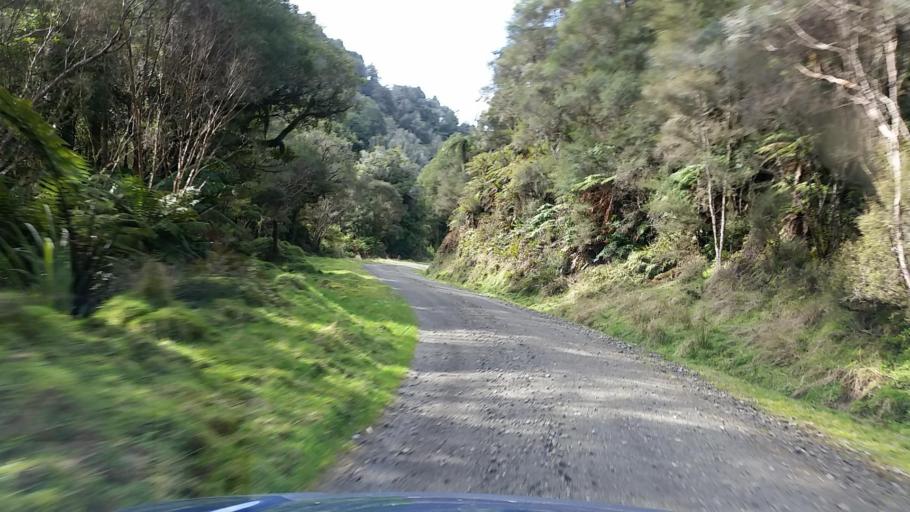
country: NZ
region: Taranaki
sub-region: South Taranaki District
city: Eltham
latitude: -39.2604
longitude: 174.7885
